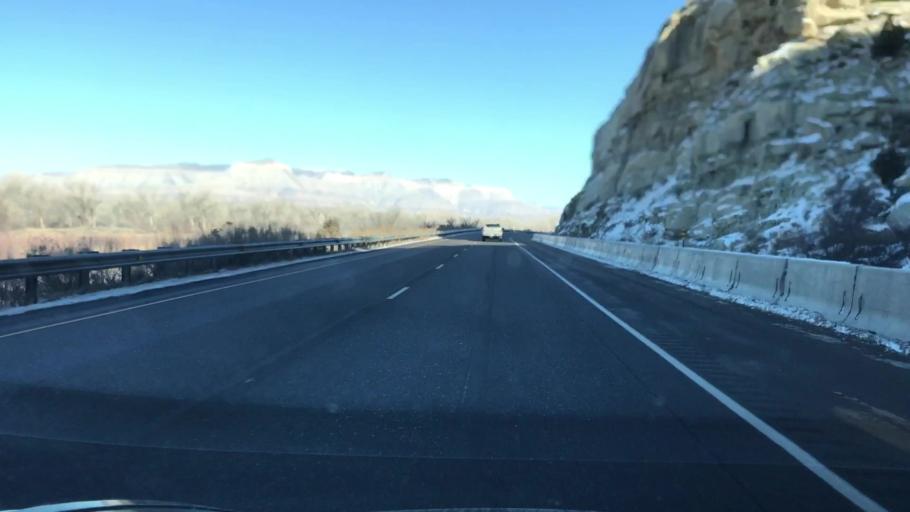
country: US
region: Colorado
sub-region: Mesa County
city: Palisade
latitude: 39.2757
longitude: -108.2422
